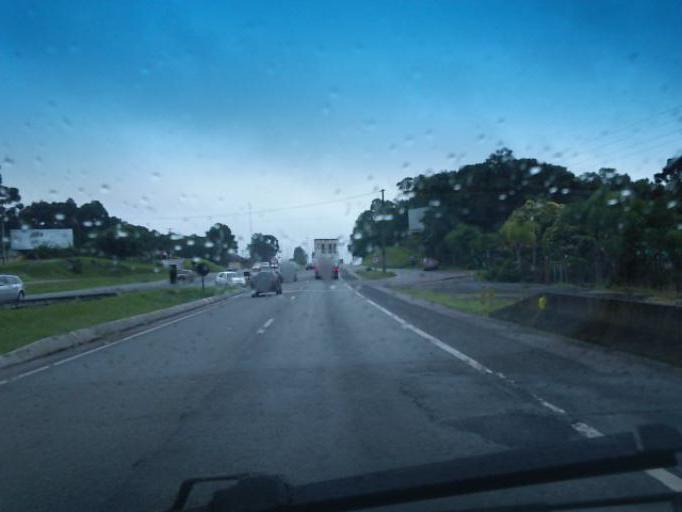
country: BR
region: Parana
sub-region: Sao Jose Dos Pinhais
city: Sao Jose dos Pinhais
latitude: -25.7189
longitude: -49.1374
